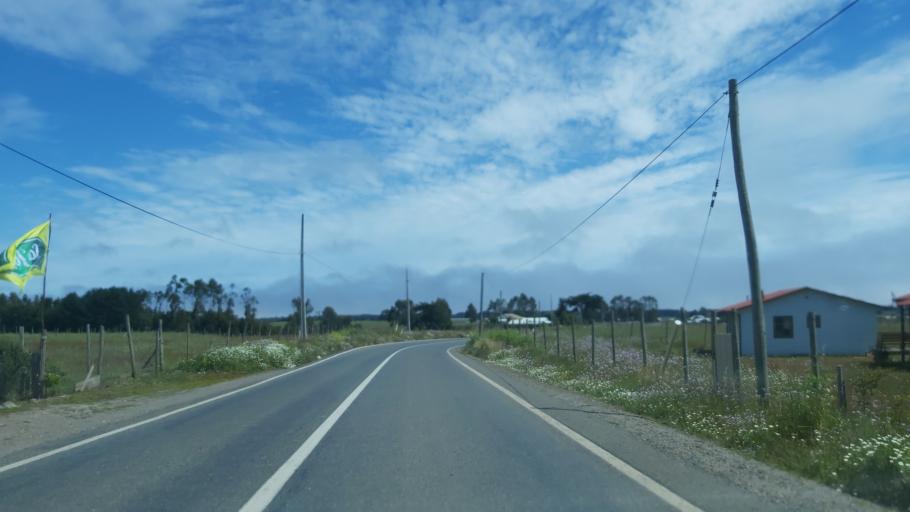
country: CL
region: Maule
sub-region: Provincia de Talca
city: Constitucion
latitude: -35.5823
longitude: -72.6017
